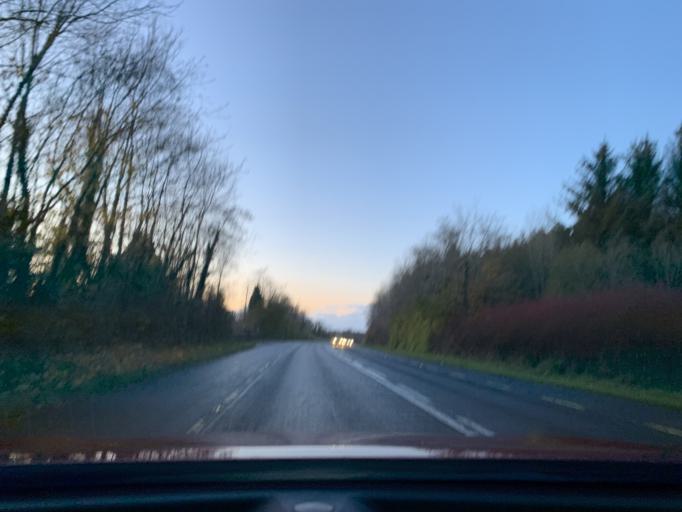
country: IE
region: Connaught
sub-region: County Leitrim
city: Carrick-on-Shannon
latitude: 53.9360
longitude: -8.0533
